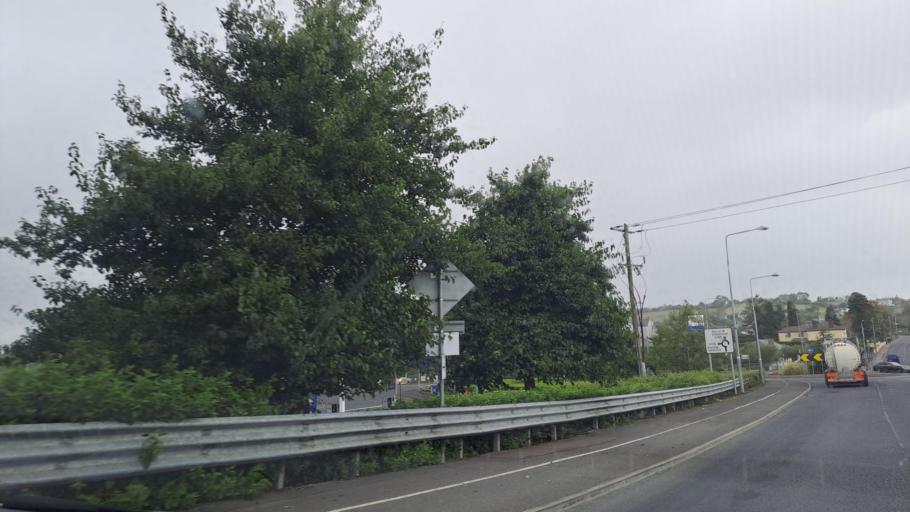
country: IE
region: Ulster
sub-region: An Cabhan
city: Bailieborough
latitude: 53.9170
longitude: -6.9677
